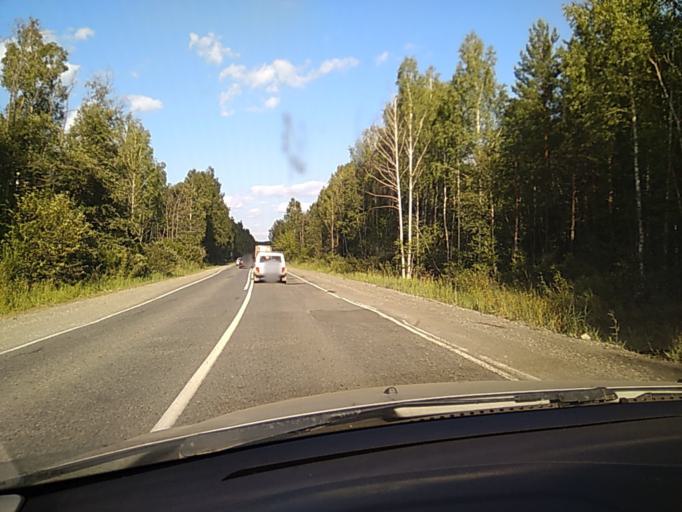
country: RU
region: Chelyabinsk
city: Karabash
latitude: 55.4994
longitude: 60.2964
